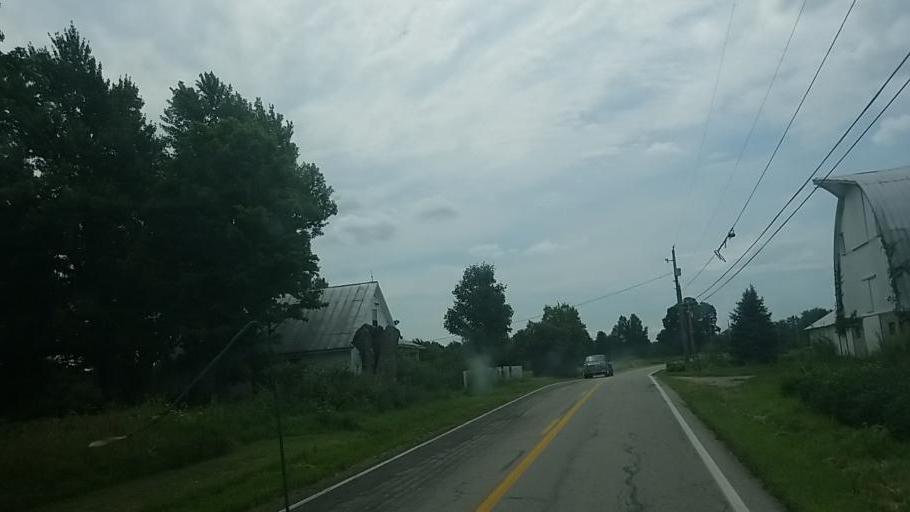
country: US
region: Ohio
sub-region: Franklin County
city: New Albany
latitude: 40.1364
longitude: -82.8213
